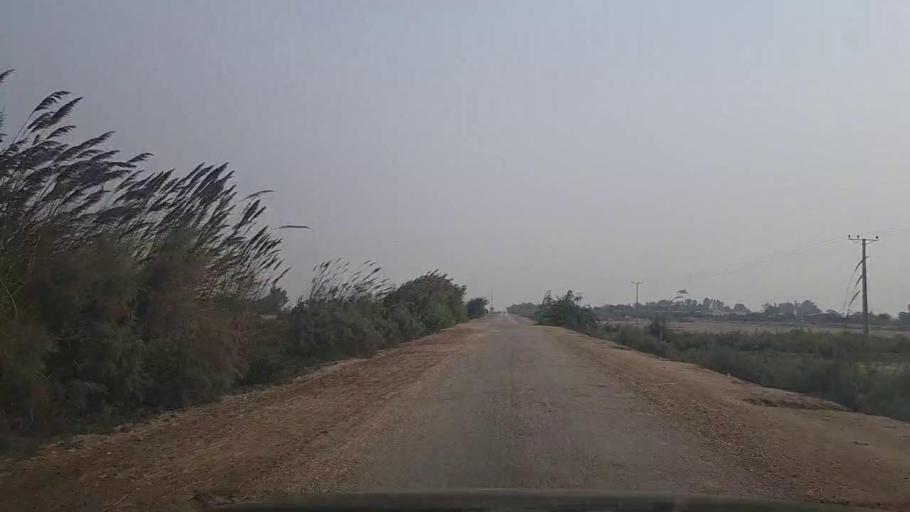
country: PK
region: Sindh
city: Mirpur Sakro
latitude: 24.4719
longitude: 67.6725
